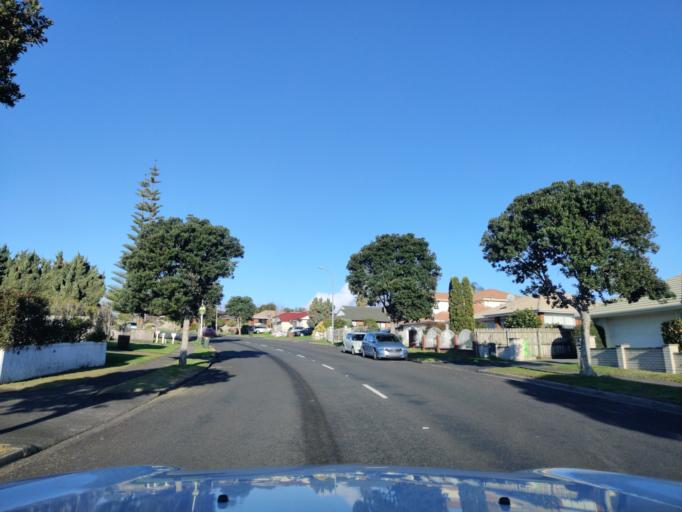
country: NZ
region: Auckland
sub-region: Auckland
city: Pakuranga
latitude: -36.9176
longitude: 174.9208
